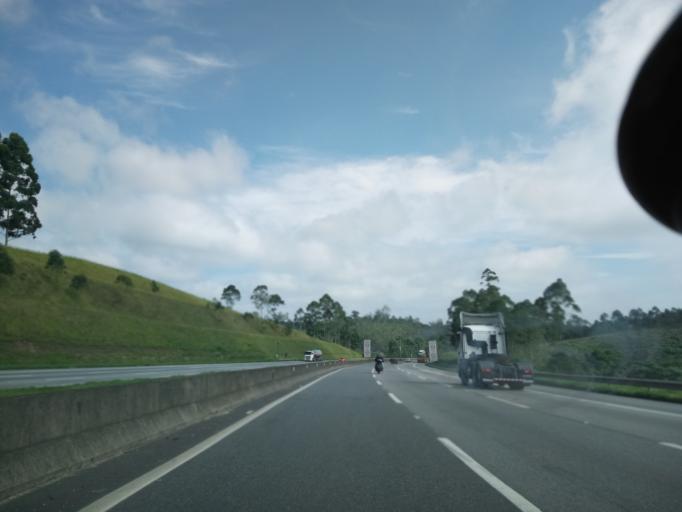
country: BR
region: Sao Paulo
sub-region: Itapecerica Da Serra
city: Itapecerica da Serra
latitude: -23.7426
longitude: -46.8130
